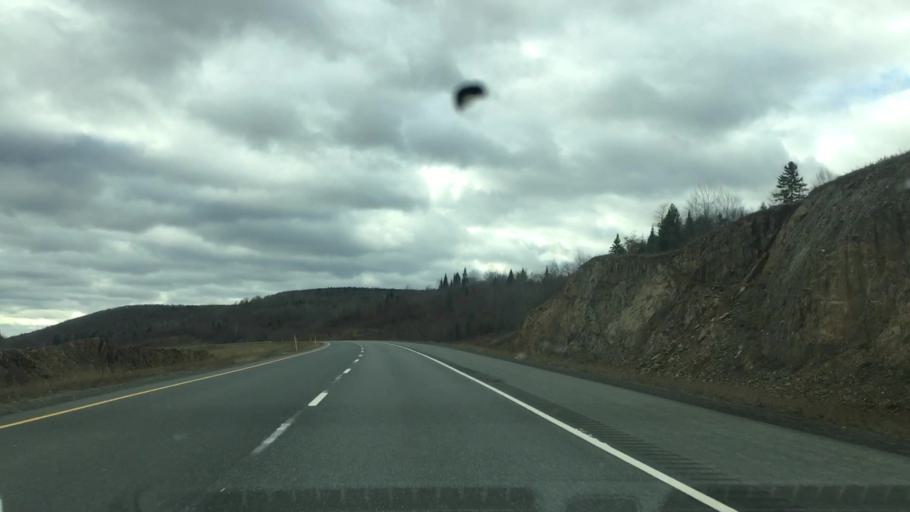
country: US
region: Maine
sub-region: Aroostook County
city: Fort Fairfield
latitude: 46.7013
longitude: -67.7400
